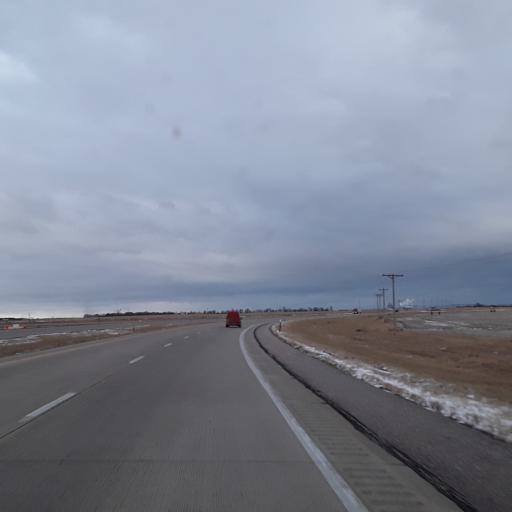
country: US
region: Nebraska
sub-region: Fillmore County
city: Geneva
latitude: 40.5614
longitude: -97.5948
